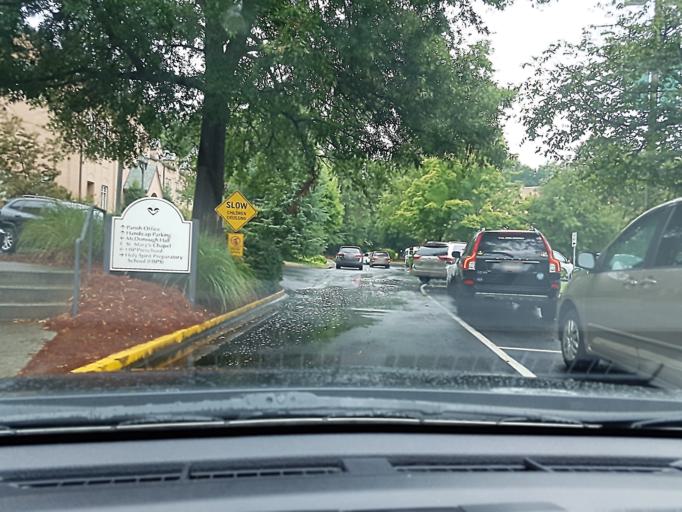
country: US
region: Georgia
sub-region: Cobb County
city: Vinings
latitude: 33.8770
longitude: -84.4111
